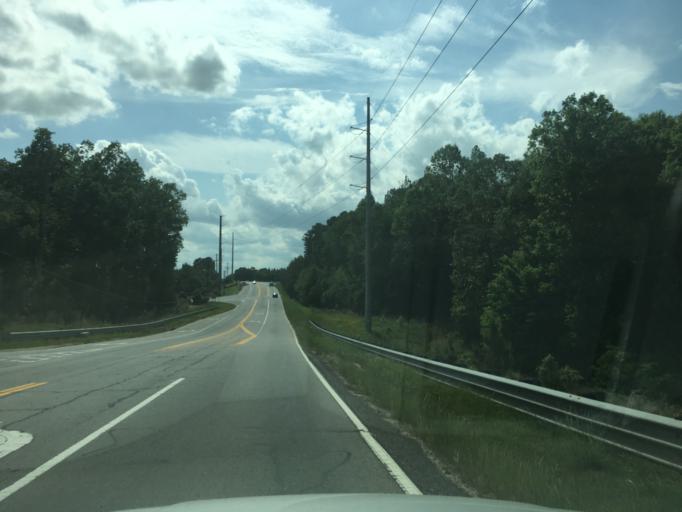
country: US
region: Georgia
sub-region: Jackson County
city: Braselton
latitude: 34.1052
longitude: -83.7772
